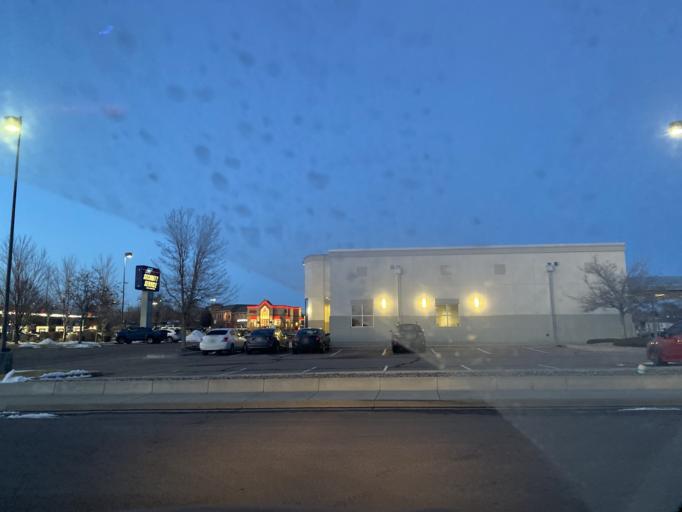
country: US
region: Colorado
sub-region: El Paso County
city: Security-Widefield
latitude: 38.7171
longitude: -104.6971
